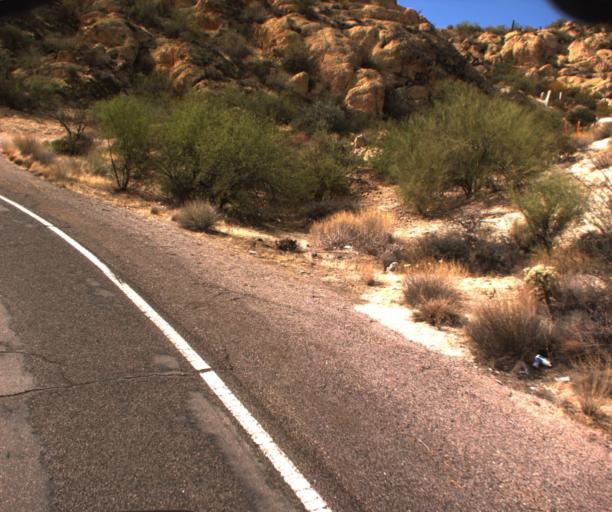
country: US
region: Arizona
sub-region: Pinal County
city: Apache Junction
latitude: 33.5353
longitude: -111.4548
